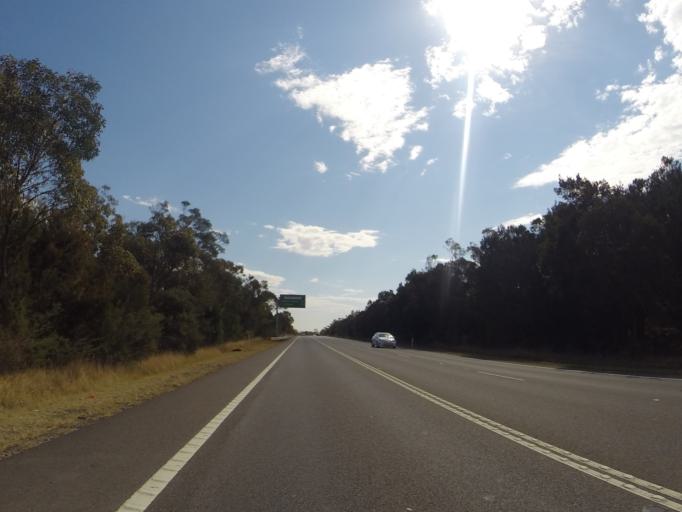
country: AU
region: New South Wales
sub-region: Sutherland Shire
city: Engadine
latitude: -34.0479
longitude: 150.9618
